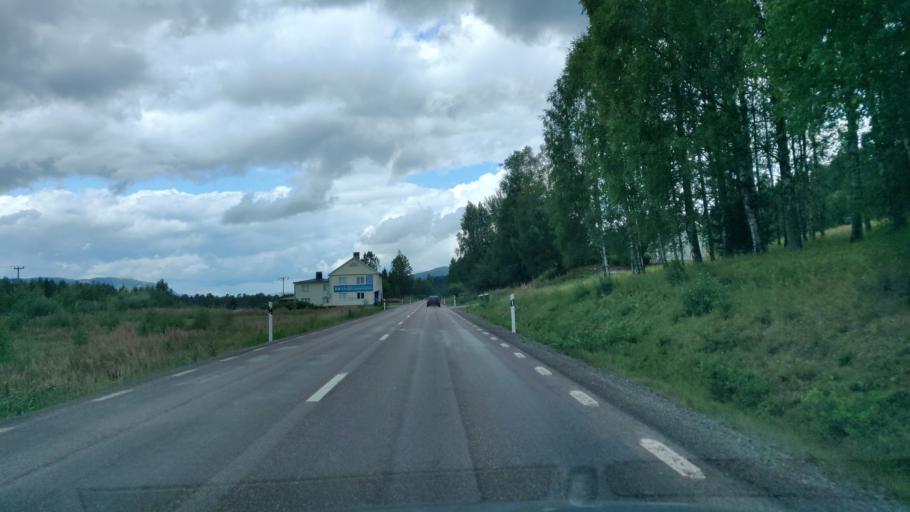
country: SE
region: Vaermland
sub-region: Torsby Kommun
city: Torsby
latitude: 60.5899
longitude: 13.0762
